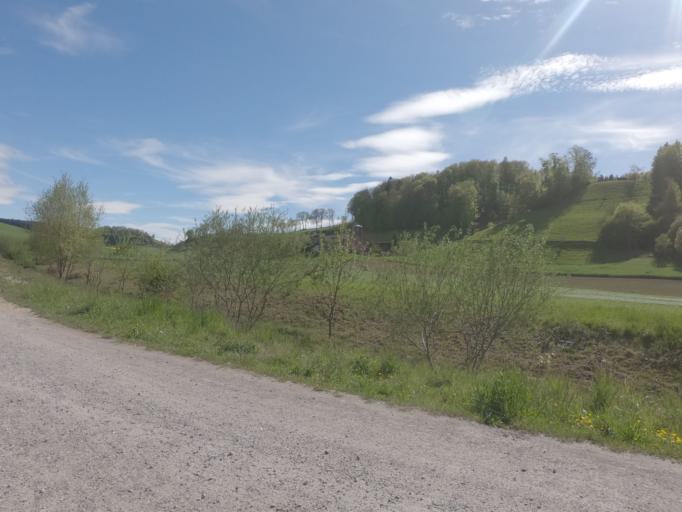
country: CH
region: Bern
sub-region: Bern-Mittelland District
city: Vechigen
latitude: 46.9386
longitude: 7.5514
